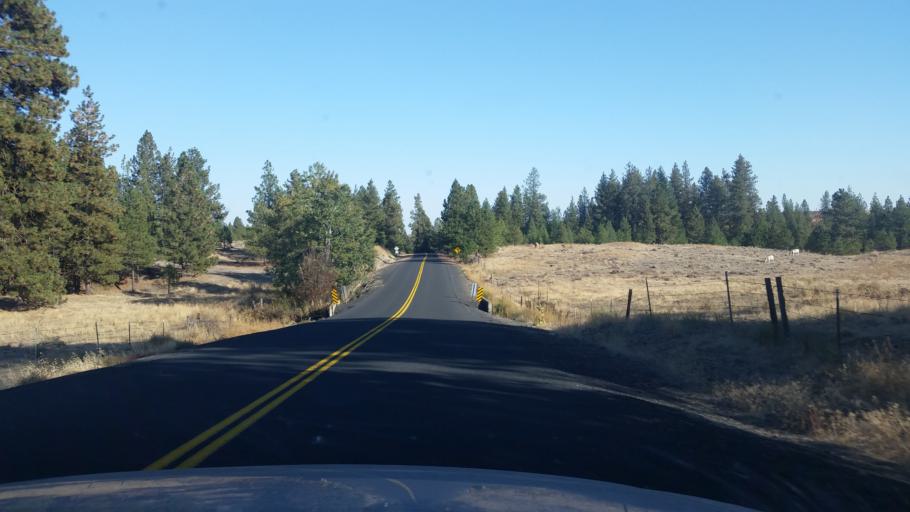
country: US
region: Washington
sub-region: Spokane County
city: Cheney
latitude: 47.3597
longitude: -117.6981
